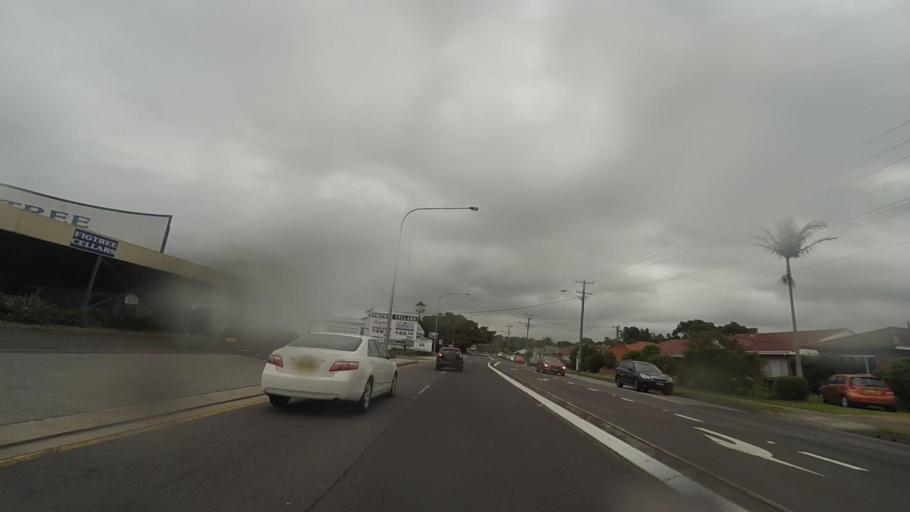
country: AU
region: New South Wales
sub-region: Wollongong
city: West Wollongong
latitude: -34.4322
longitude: 150.8653
